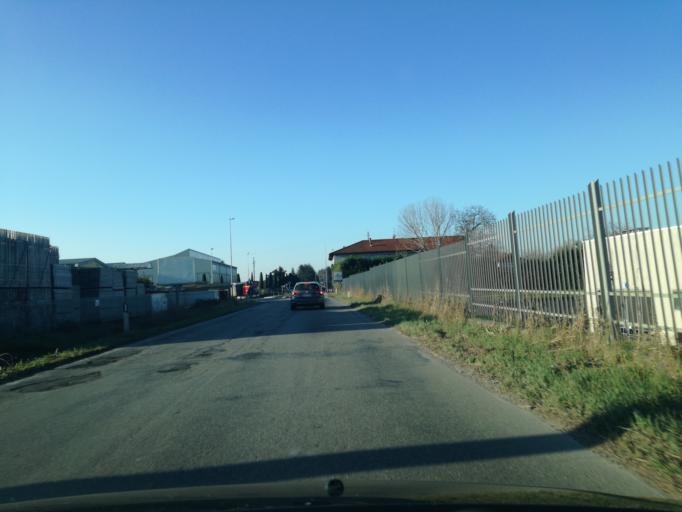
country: IT
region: Lombardy
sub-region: Provincia di Lecco
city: Verderio Inferiore
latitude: 45.6664
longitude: 9.4205
